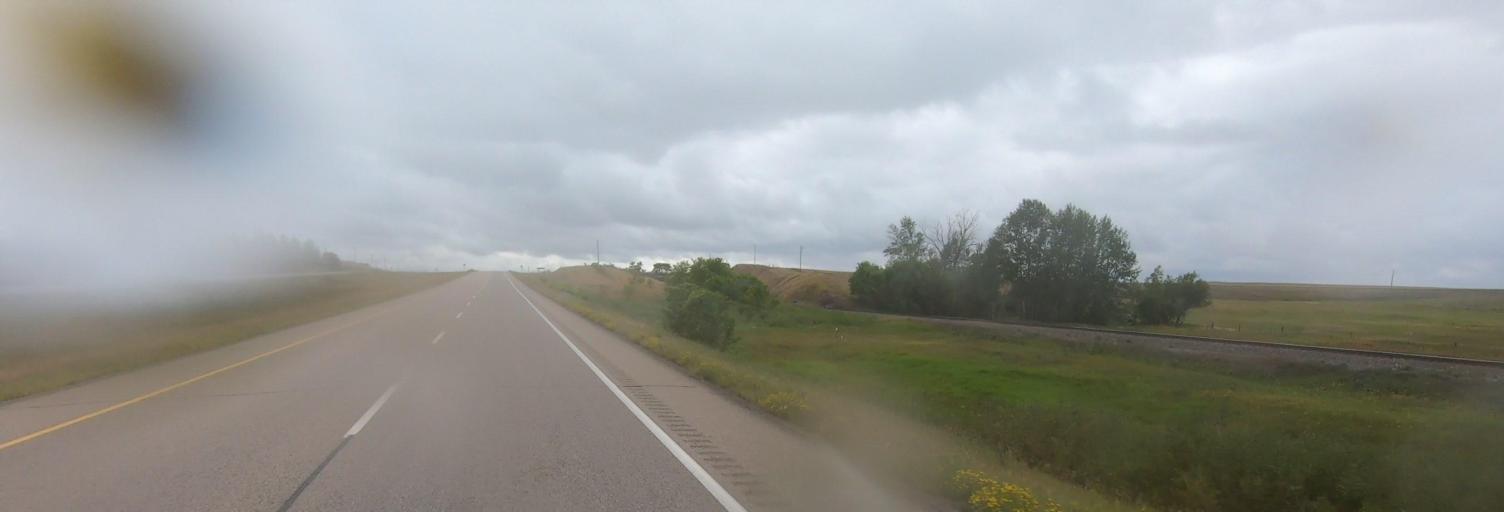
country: CA
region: Saskatchewan
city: Swift Current
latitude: 50.3818
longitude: -107.4898
